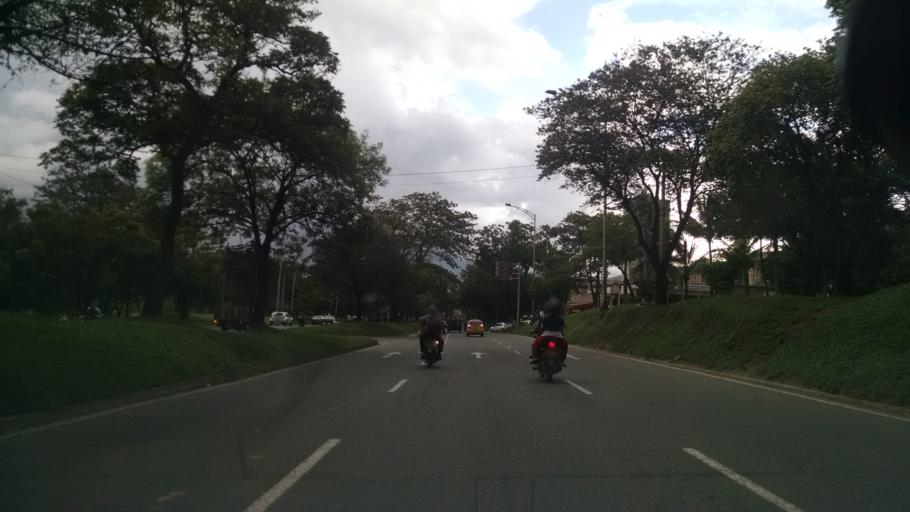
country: CO
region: Antioquia
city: Medellin
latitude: 6.2613
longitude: -75.5729
